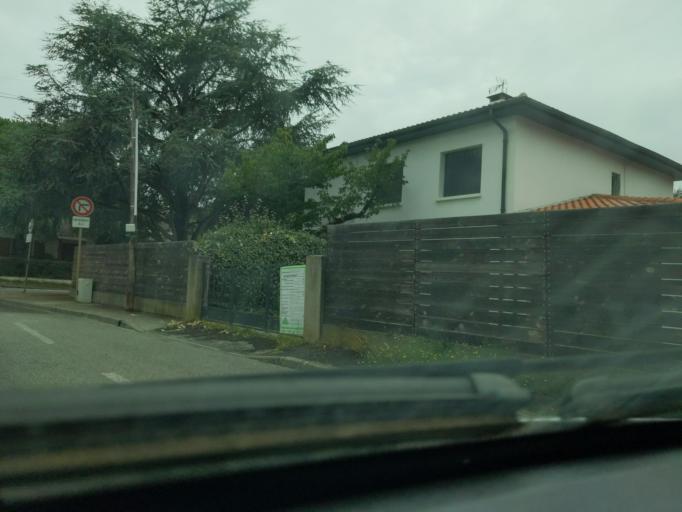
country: FR
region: Midi-Pyrenees
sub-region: Departement de la Haute-Garonne
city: Colomiers
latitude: 43.5893
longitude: 1.3591
